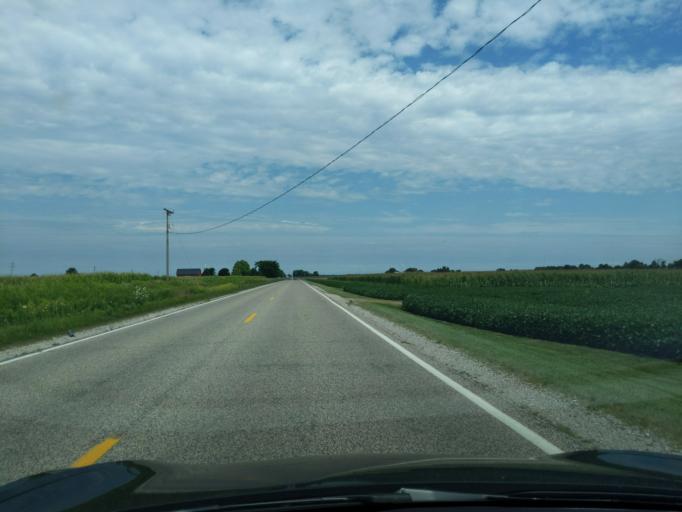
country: US
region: Michigan
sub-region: Gratiot County
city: Breckenridge
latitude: 43.3552
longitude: -84.4298
